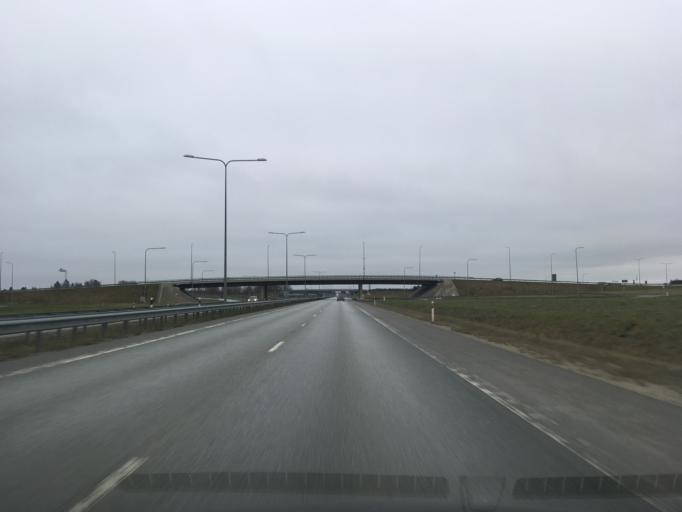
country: EE
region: Laeaene-Virumaa
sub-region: Haljala vald
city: Haljala
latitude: 59.4243
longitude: 26.2663
